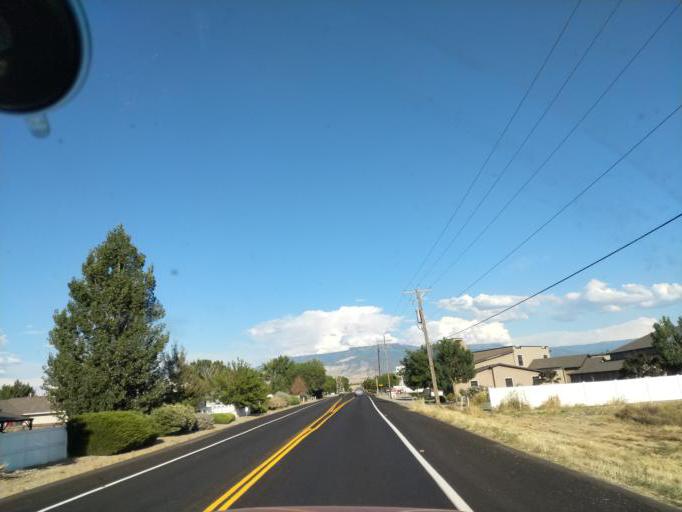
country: US
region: Colorado
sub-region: Mesa County
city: Fruitvale
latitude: 39.0629
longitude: -108.4682
